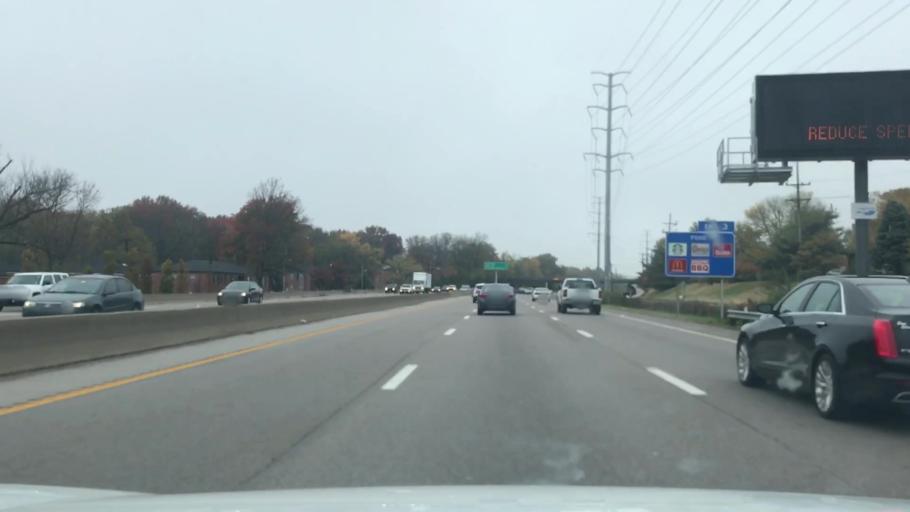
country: US
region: Missouri
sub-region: Saint Louis County
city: Olivette
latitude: 38.6645
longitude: -90.3596
